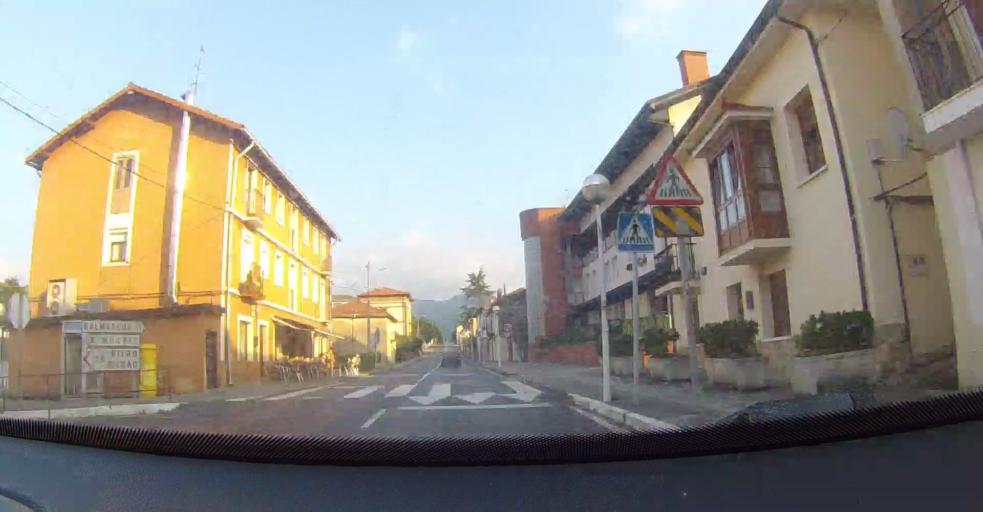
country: ES
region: Basque Country
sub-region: Bizkaia
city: Sopuerta
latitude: 43.2741
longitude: -3.1567
